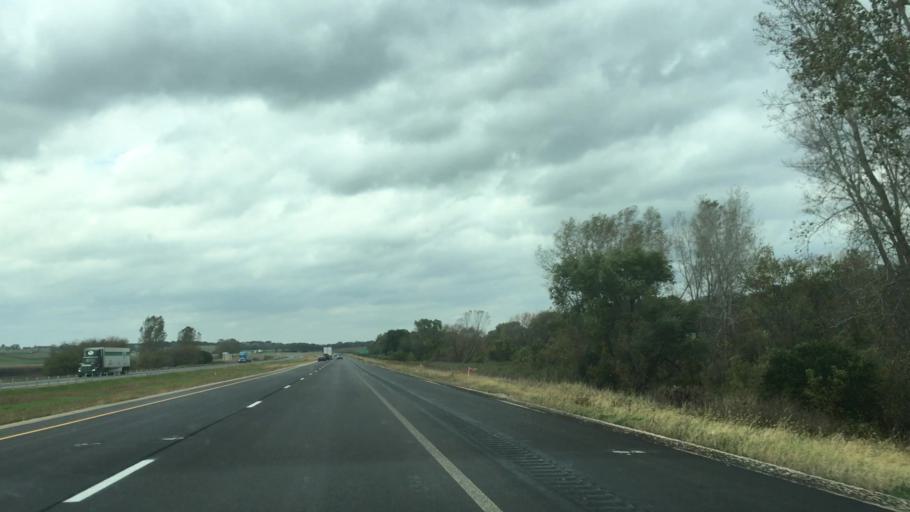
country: US
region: Minnesota
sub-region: Olmsted County
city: Rochester
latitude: 43.9659
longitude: -92.3936
